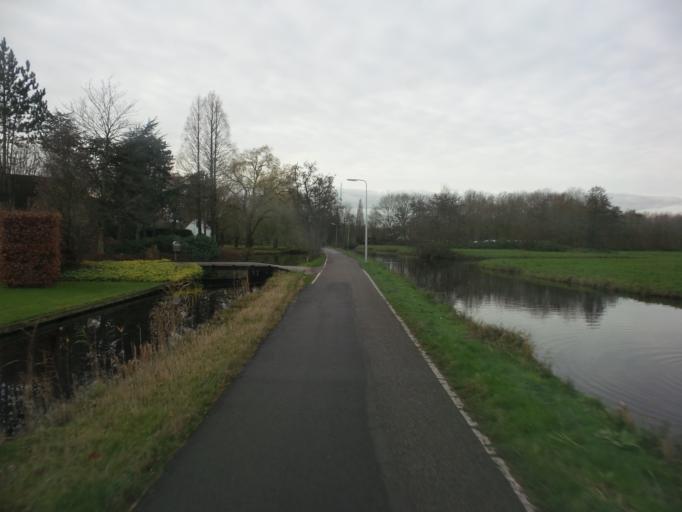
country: NL
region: South Holland
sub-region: Gemeente Vlist
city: Haastrecht
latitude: 52.0164
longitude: 4.7447
